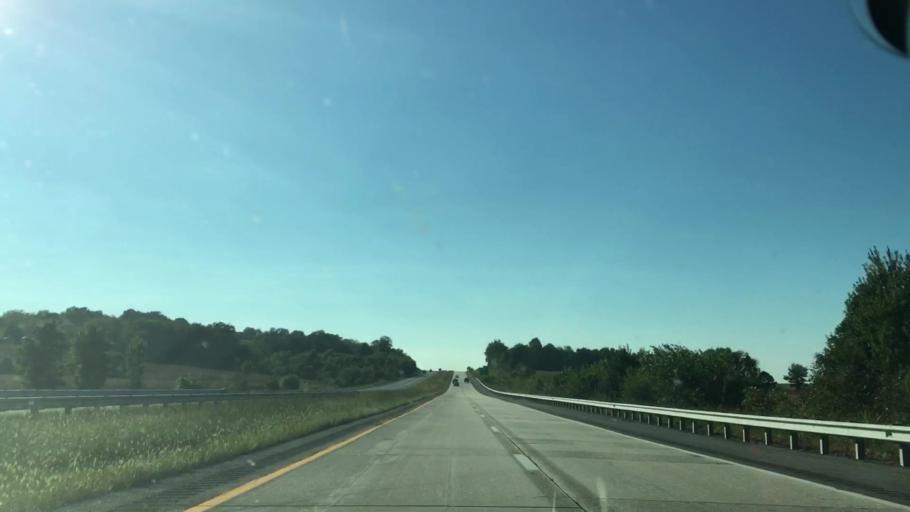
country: US
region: Kentucky
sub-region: Henderson County
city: Henderson
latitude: 37.7811
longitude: -87.4564
